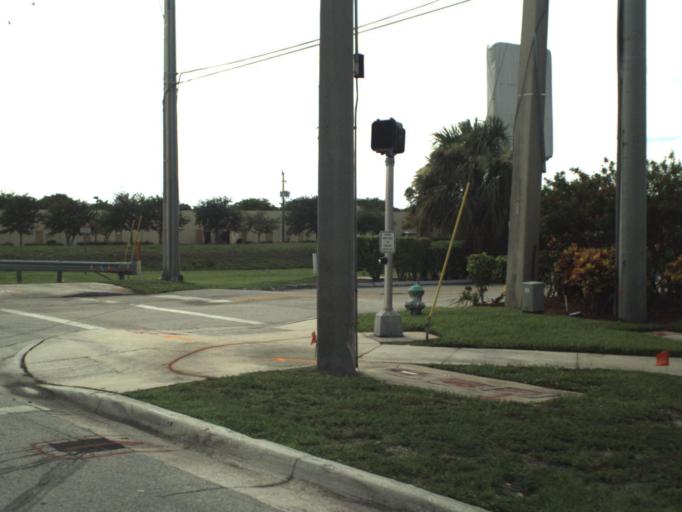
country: US
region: Florida
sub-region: Palm Beach County
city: Mangonia Park
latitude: 26.7588
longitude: -80.0889
